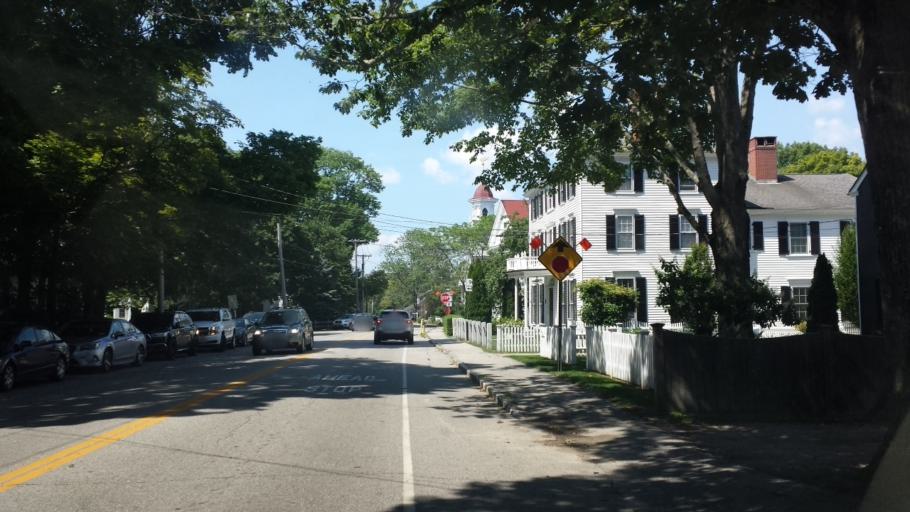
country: US
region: Maine
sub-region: York County
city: Kennebunkport
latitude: 43.3621
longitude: -70.4753
